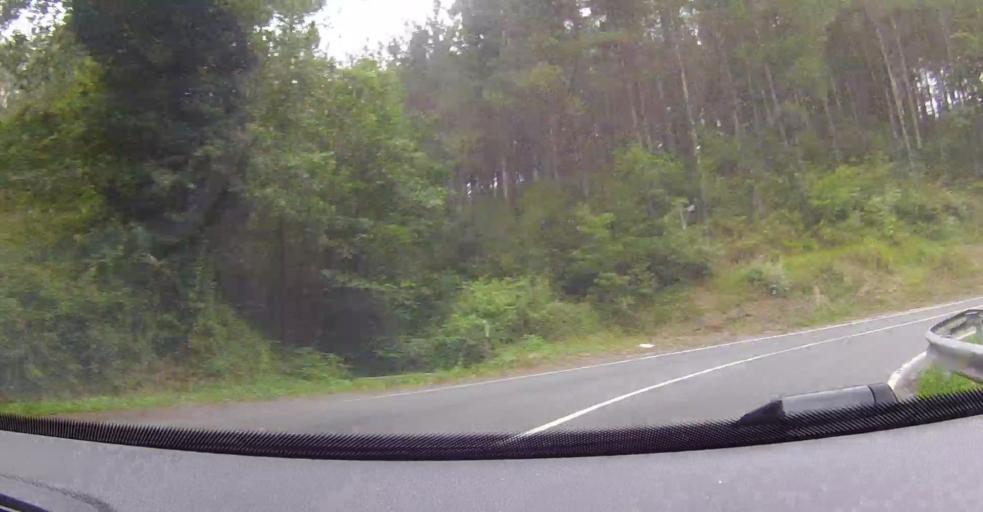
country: ES
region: Basque Country
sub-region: Bizkaia
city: Balmaseda
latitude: 43.2399
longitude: -3.2293
